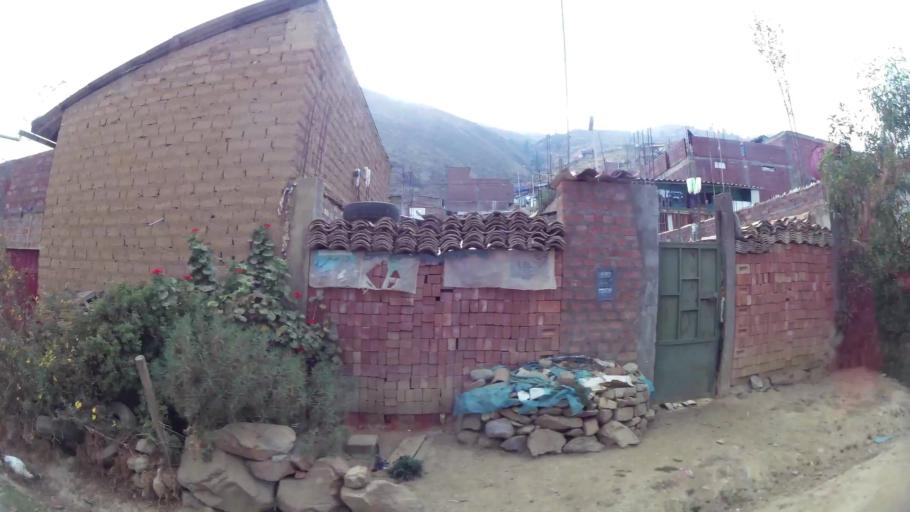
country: PE
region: Junin
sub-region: Provincia de Huancayo
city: Huancayo
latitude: -12.0516
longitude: -75.1860
